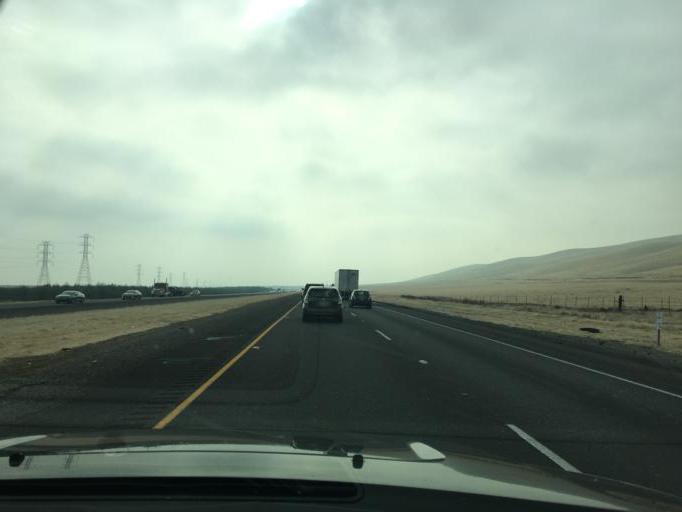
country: US
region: California
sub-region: Merced County
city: South Dos Palos
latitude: 36.8809
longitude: -120.7952
